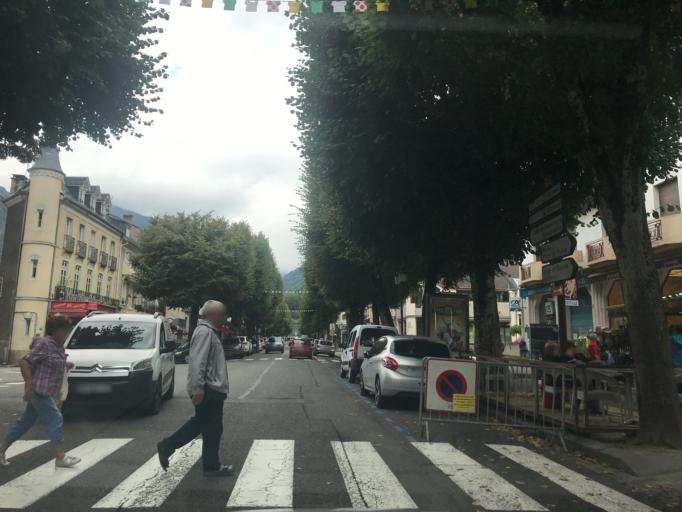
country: FR
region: Midi-Pyrenees
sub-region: Departement de la Haute-Garonne
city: Bagneres-de-Luchon
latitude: 42.7890
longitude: 0.5922
